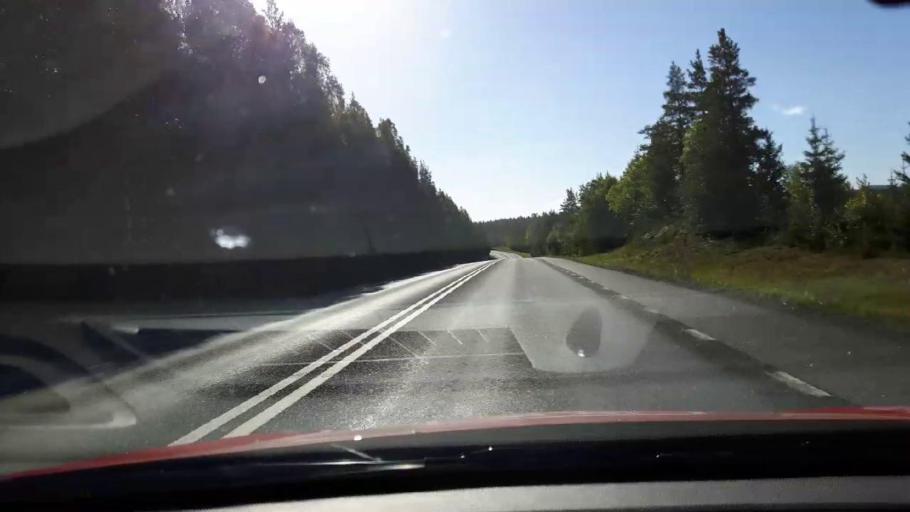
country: SE
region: Jaemtland
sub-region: Braecke Kommun
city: Braecke
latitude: 62.7196
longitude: 15.4525
